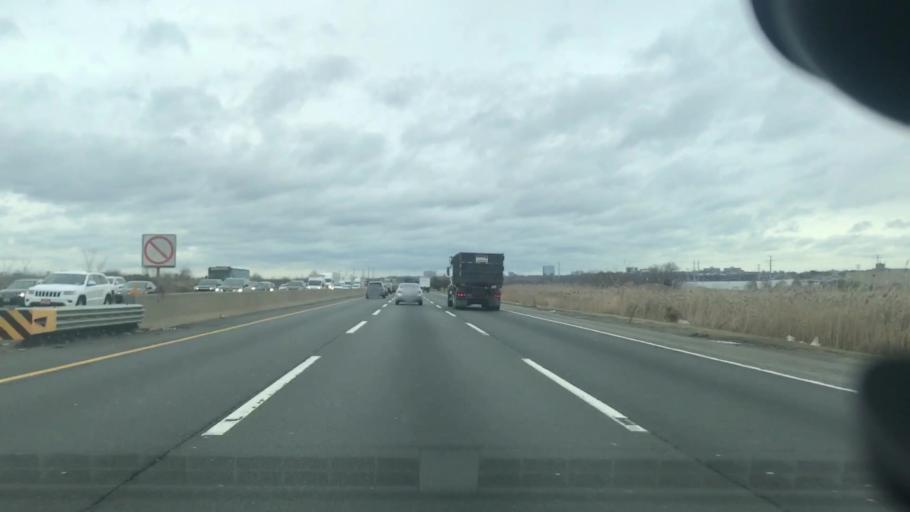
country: US
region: New Jersey
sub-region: Hudson County
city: Secaucus
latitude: 40.7966
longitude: -74.0409
